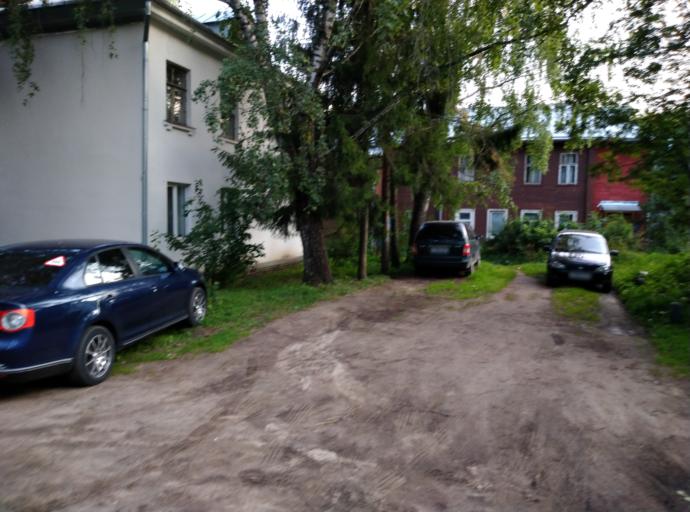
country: RU
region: Kostroma
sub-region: Kostromskoy Rayon
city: Kostroma
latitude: 57.7638
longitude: 40.9316
